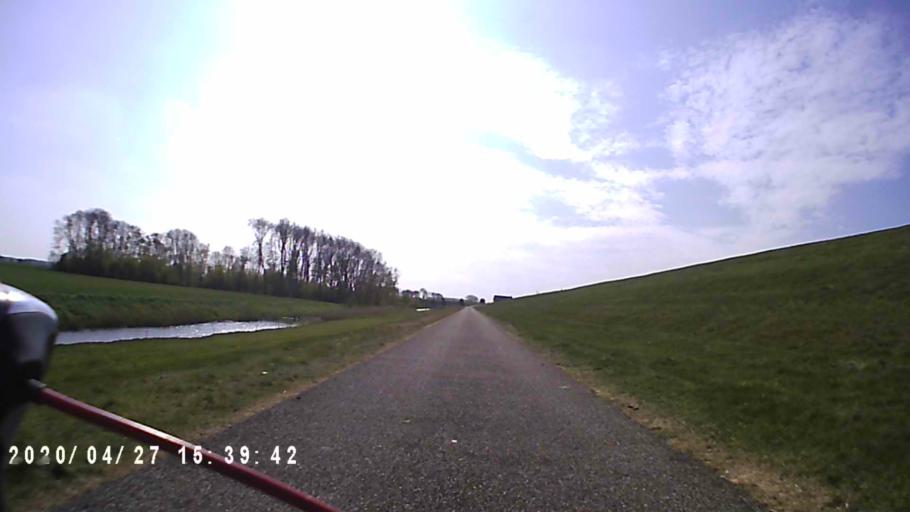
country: NL
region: Groningen
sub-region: Gemeente De Marne
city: Ulrum
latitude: 53.3934
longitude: 6.3125
